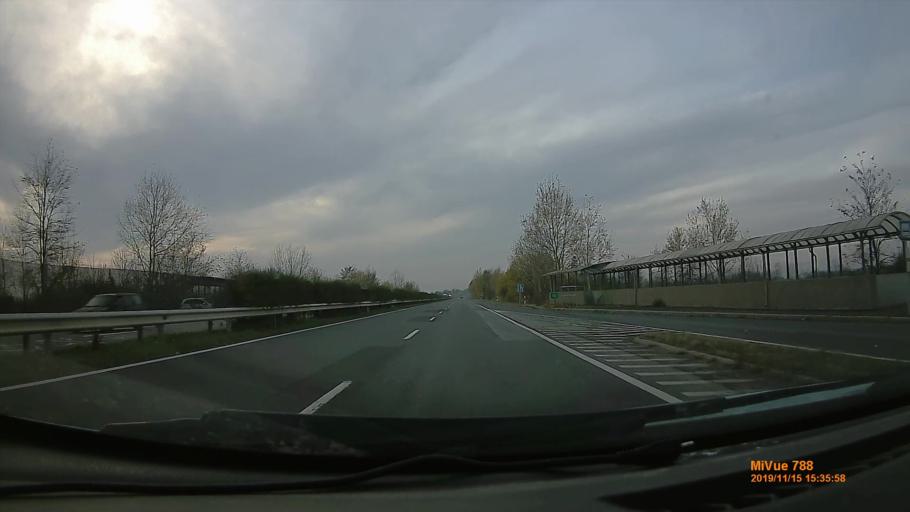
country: HU
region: Bekes
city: Gyula
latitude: 46.6560
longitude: 21.2204
